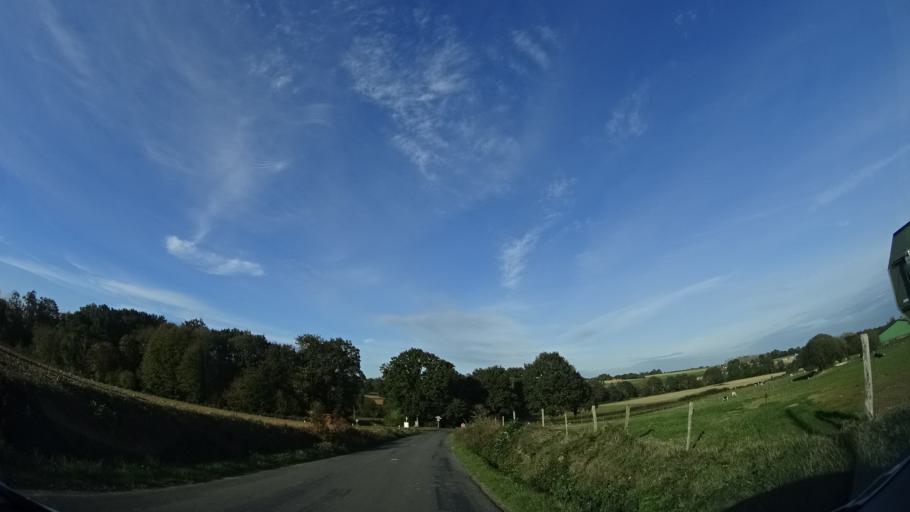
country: FR
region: Brittany
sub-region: Departement d'Ille-et-Vilaine
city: Geveze
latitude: 48.2152
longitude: -1.8269
